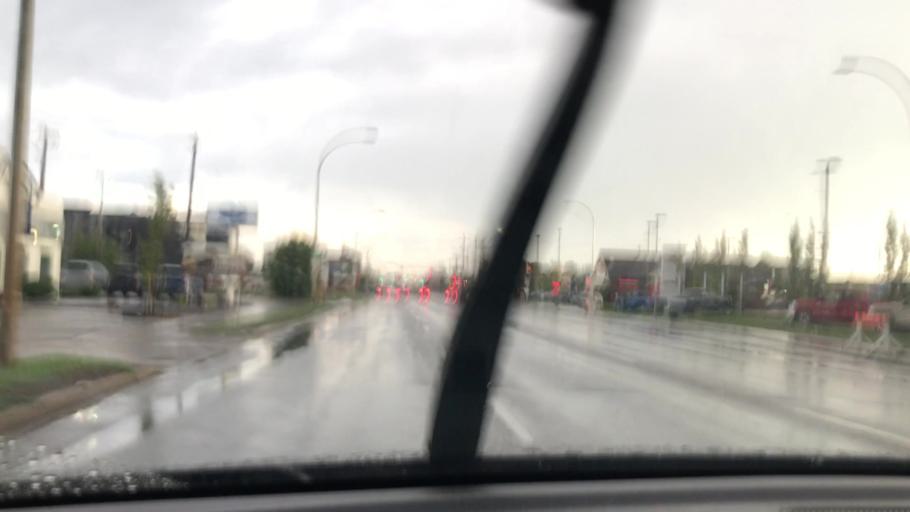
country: CA
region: Alberta
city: Edmonton
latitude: 53.4900
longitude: -113.4948
